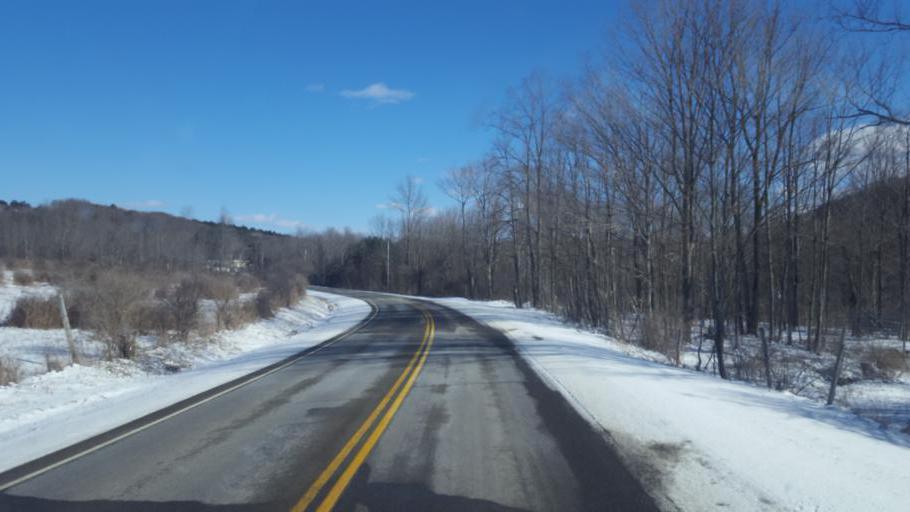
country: US
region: New York
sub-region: Allegany County
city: Belmont
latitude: 42.1735
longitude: -78.0663
